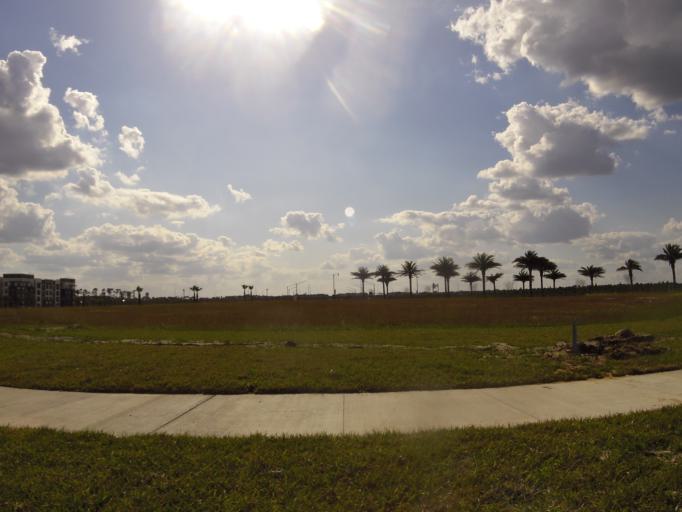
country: US
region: Florida
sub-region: Saint Johns County
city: Palm Valley
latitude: 30.1670
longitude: -81.5060
